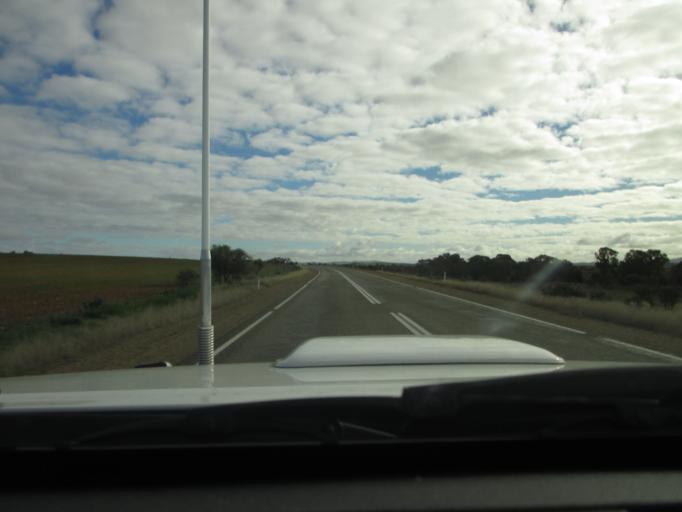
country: AU
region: South Australia
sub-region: Flinders Ranges
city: Quorn
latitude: -32.4158
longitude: 138.5228
